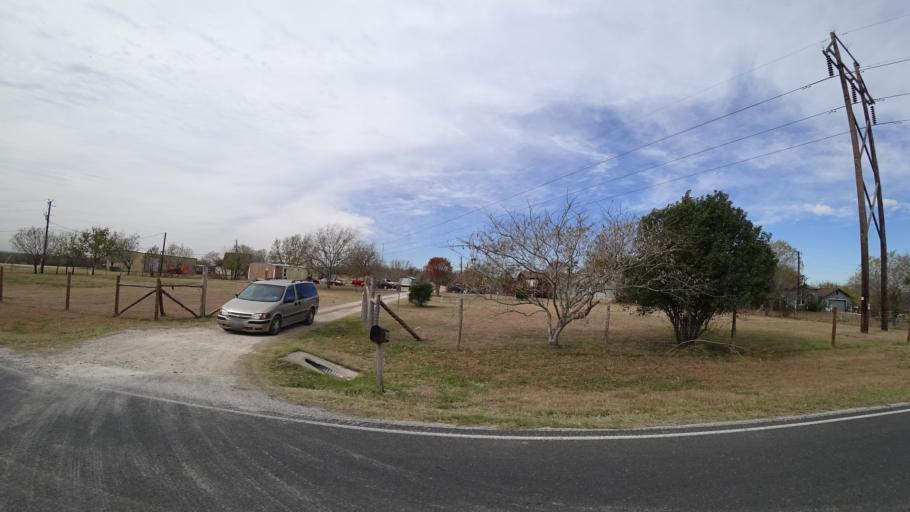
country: US
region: Texas
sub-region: Travis County
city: Garfield
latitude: 30.1406
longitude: -97.5827
